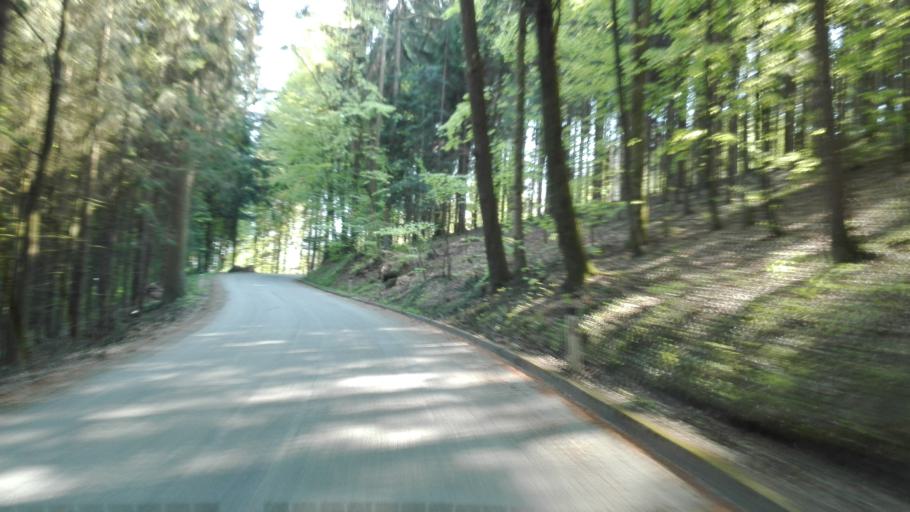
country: AT
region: Upper Austria
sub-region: Politischer Bezirk Rohrbach
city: Atzesberg
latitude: 48.4231
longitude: 13.9174
